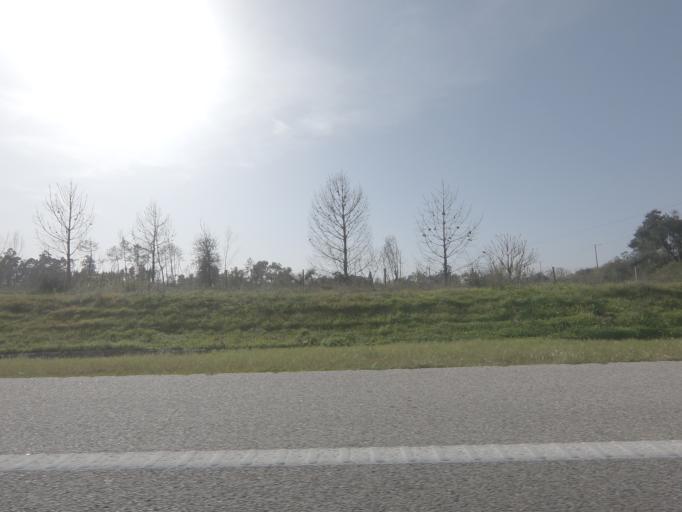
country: PT
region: Aveiro
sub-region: Mealhada
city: Mealhada
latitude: 40.4127
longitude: -8.4942
